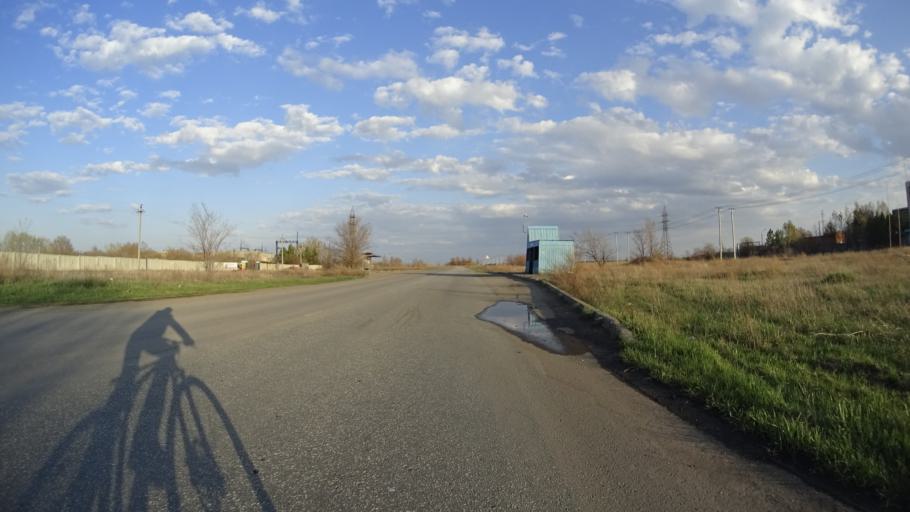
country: RU
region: Chelyabinsk
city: Troitsk
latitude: 54.0639
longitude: 61.5697
